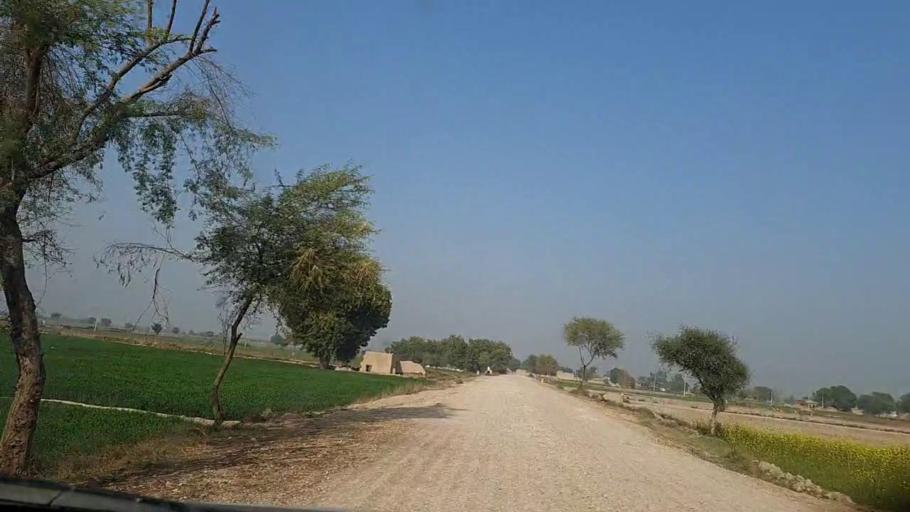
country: PK
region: Sindh
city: Moro
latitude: 26.7747
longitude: 67.9333
